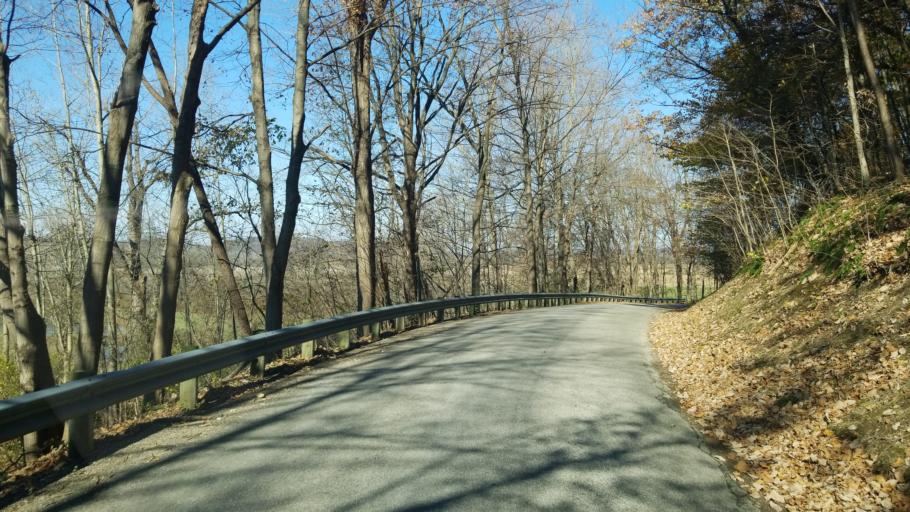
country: US
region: Ohio
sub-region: Licking County
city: Newark
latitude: 40.1475
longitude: -82.4119
